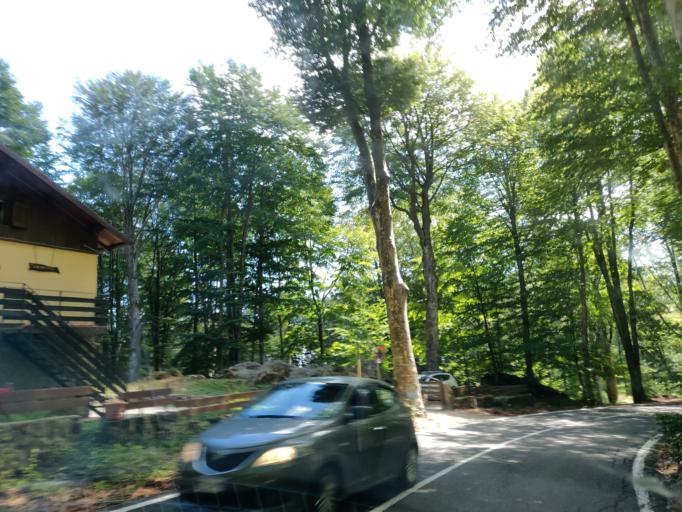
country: IT
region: Tuscany
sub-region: Provincia di Siena
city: Abbadia San Salvatore
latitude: 42.9024
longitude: 11.6378
